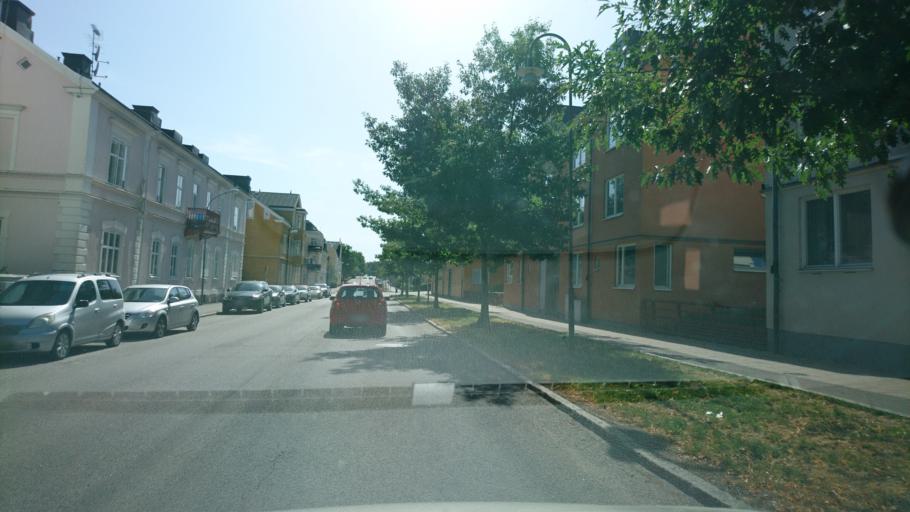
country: SE
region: Soedermanland
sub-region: Strangnas Kommun
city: Strangnas
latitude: 59.3748
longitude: 17.0269
